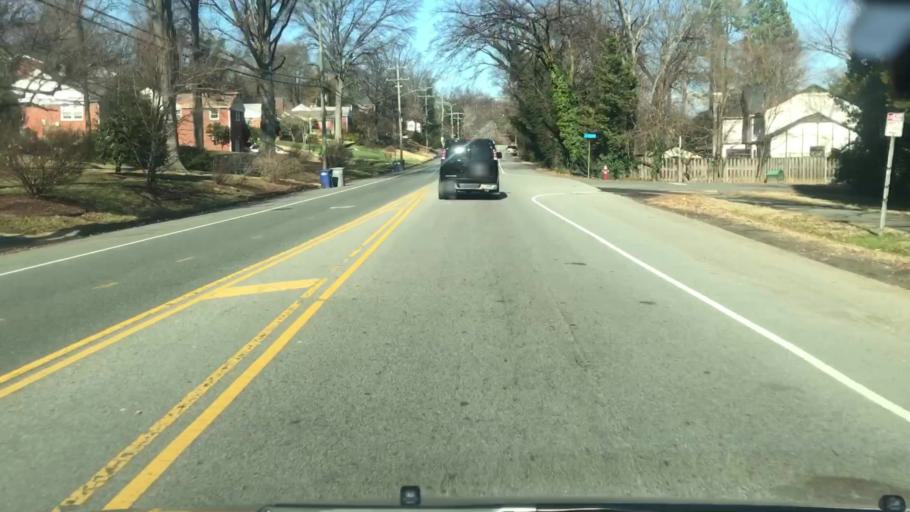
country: US
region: Virginia
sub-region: Fairfax County
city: Belle Haven
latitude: 38.7766
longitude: -77.0627
